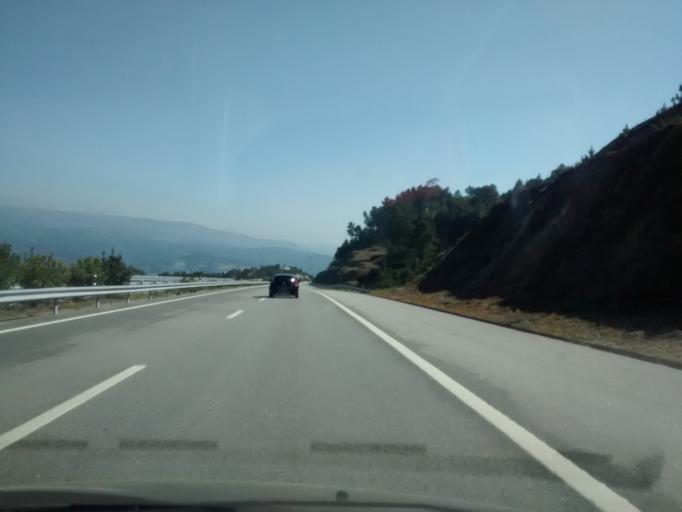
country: PT
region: Braga
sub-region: Cabeceiras de Basto
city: Refojos de Basto
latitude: 41.4676
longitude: -8.0011
